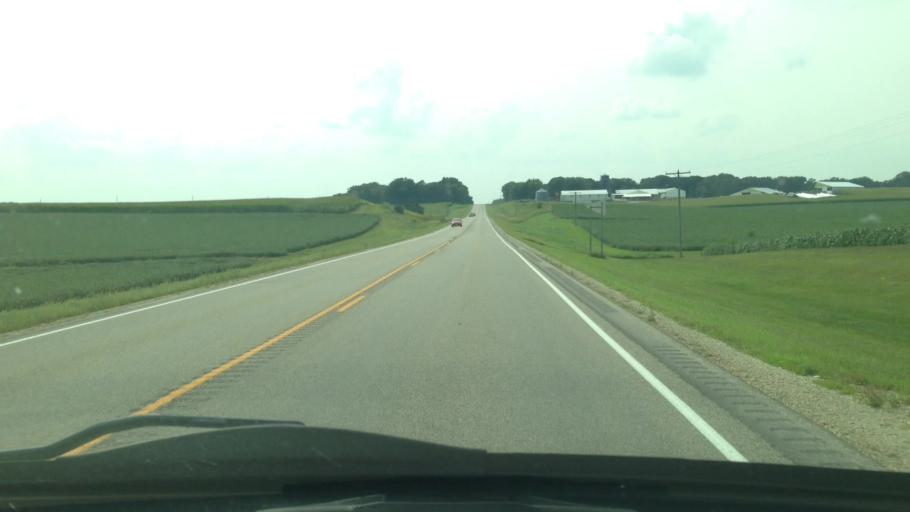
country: US
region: Minnesota
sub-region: Wabasha County
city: Plainview
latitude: 44.1652
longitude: -92.2065
